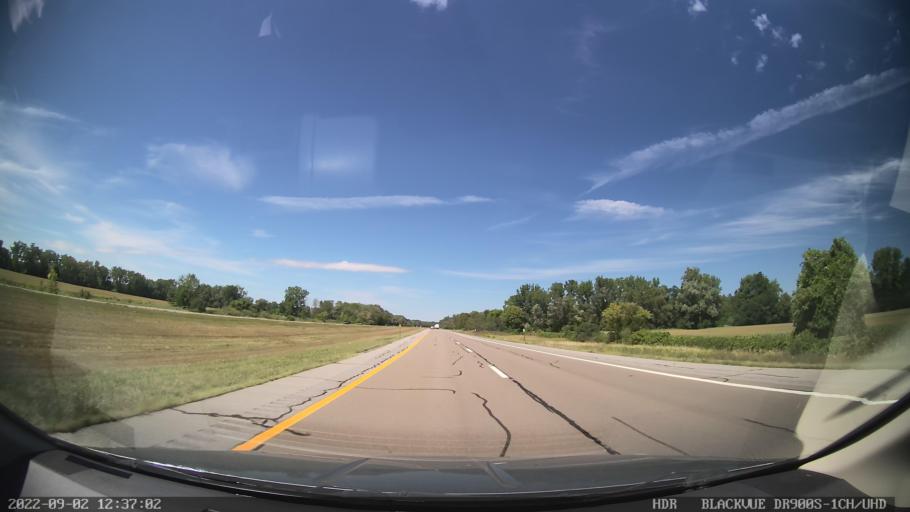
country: US
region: New York
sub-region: Livingston County
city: Mount Morris
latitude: 42.6911
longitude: -77.8037
